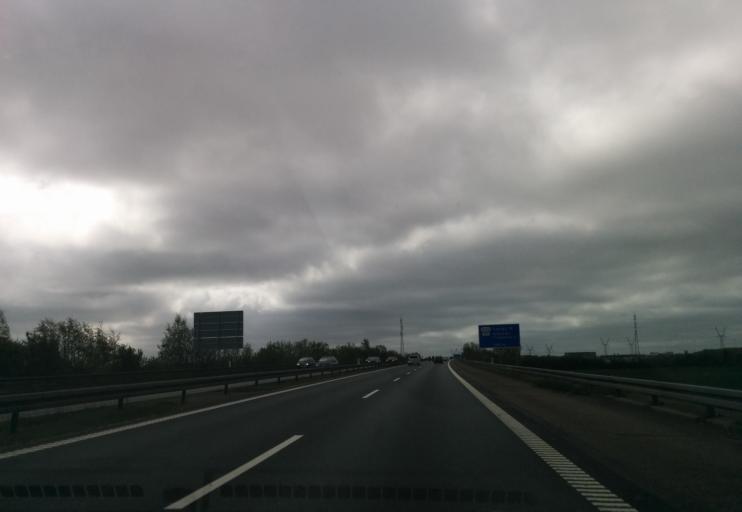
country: DK
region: South Denmark
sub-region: Fredericia Kommune
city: Taulov
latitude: 55.5521
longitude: 9.6371
